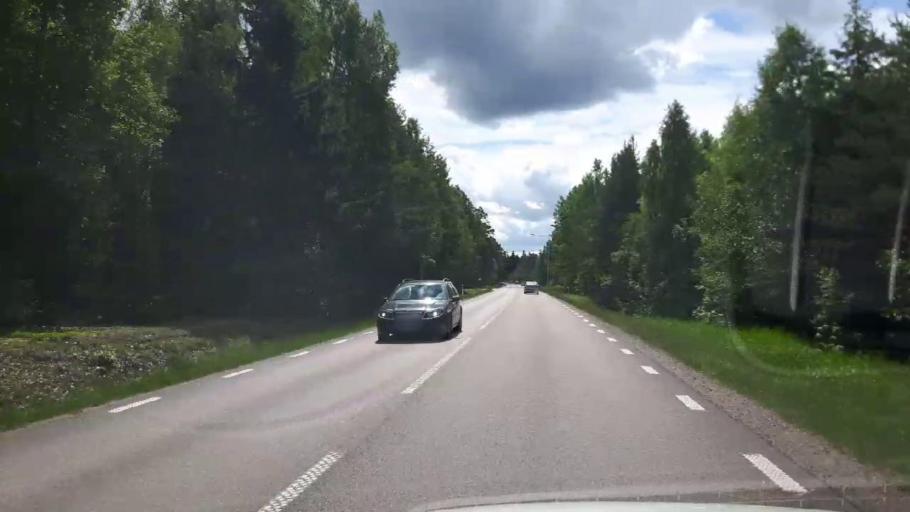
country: SE
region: Dalarna
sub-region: Faluns Kommun
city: Falun
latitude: 60.5217
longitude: 15.7342
